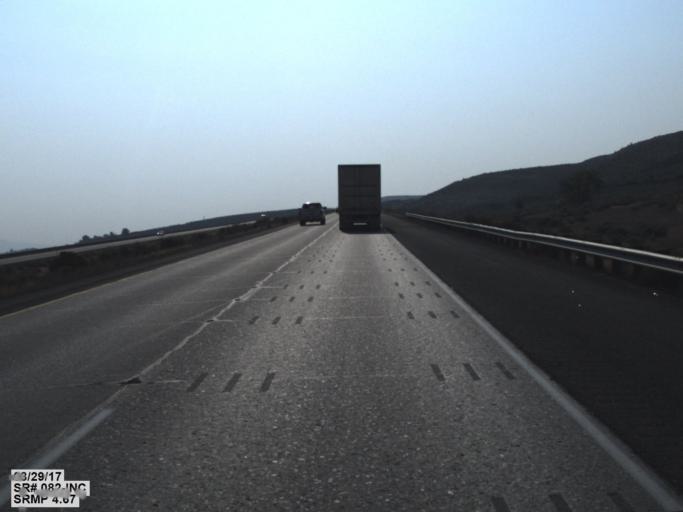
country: US
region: Washington
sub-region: Kittitas County
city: Kittitas
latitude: 46.9130
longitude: -120.4762
